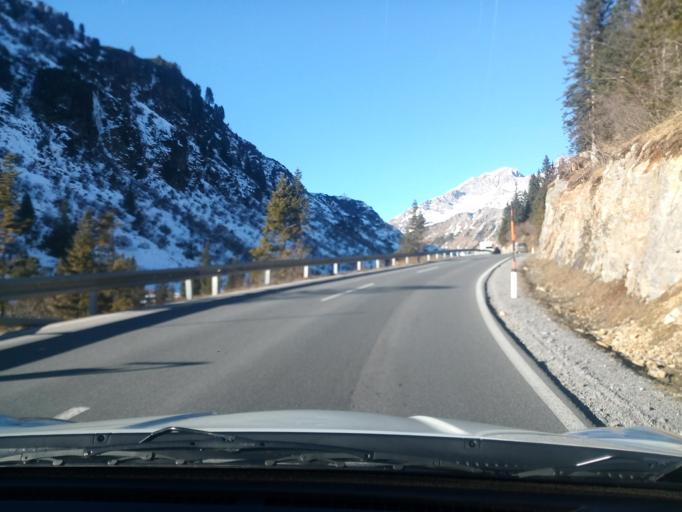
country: AT
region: Tyrol
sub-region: Politischer Bezirk Landeck
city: Sankt Anton am Arlberg
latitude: 47.1163
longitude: 10.2210
